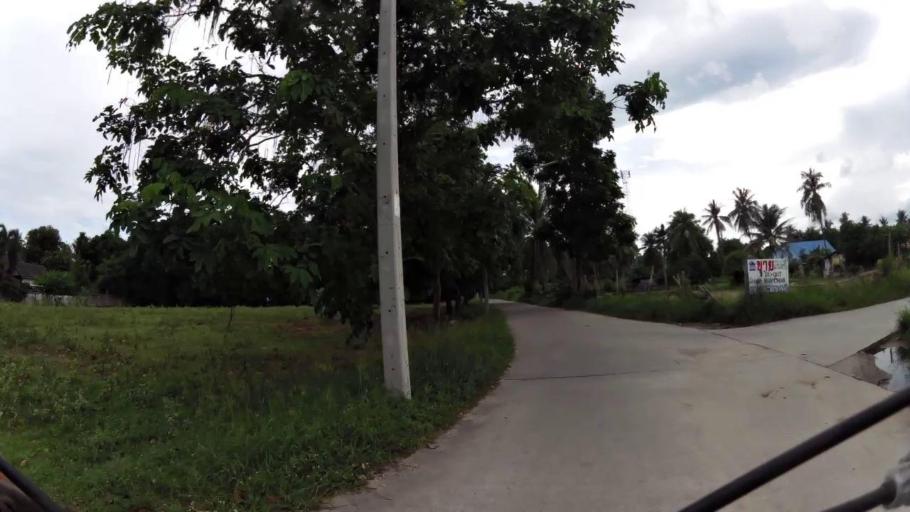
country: TH
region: Prachuap Khiri Khan
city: Prachuap Khiri Khan
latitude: 11.7408
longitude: 99.7780
